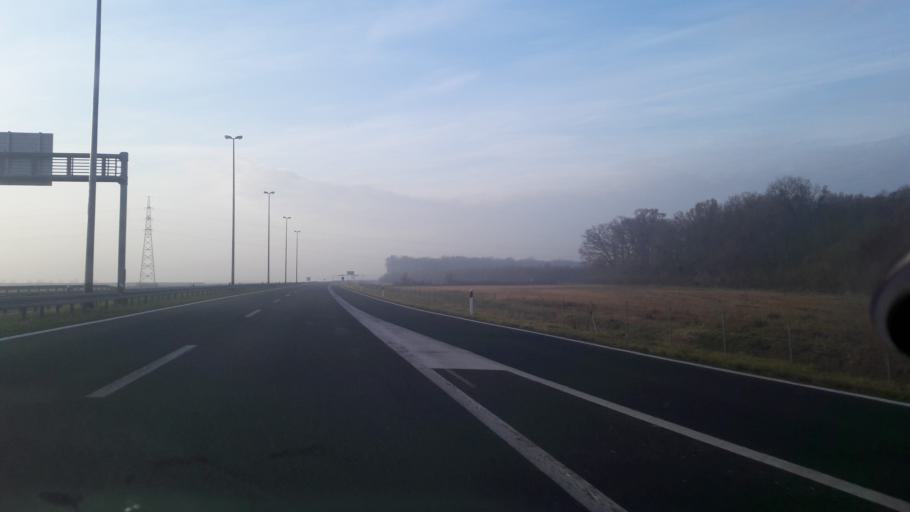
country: HR
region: Osjecko-Baranjska
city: Cepin
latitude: 45.5018
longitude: 18.5047
